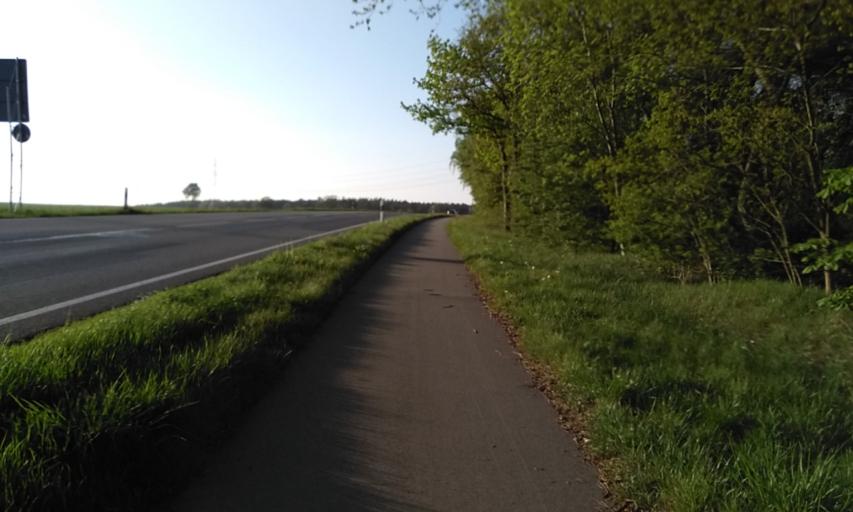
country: DE
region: Lower Saxony
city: Dollern
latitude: 53.5214
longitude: 9.5596
